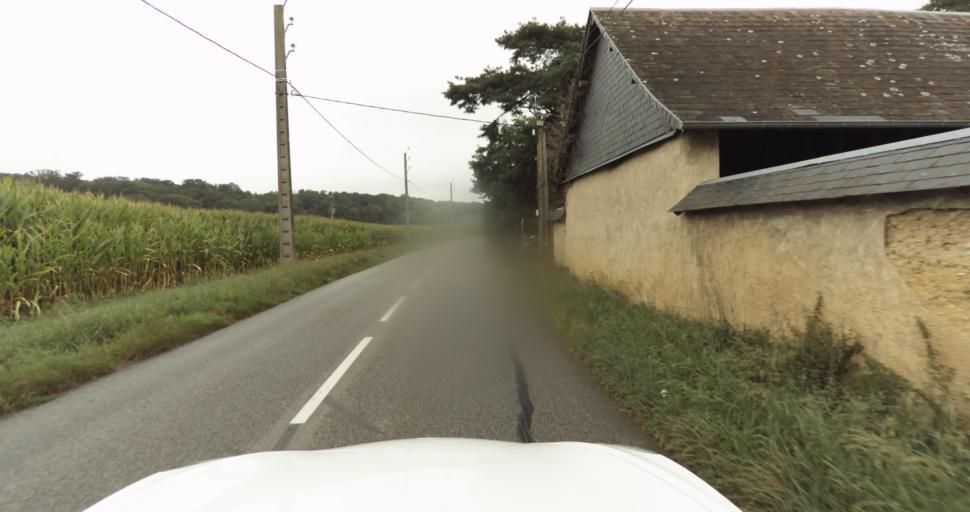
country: FR
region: Haute-Normandie
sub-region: Departement de l'Eure
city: Normanville
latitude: 49.0843
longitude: 1.1385
